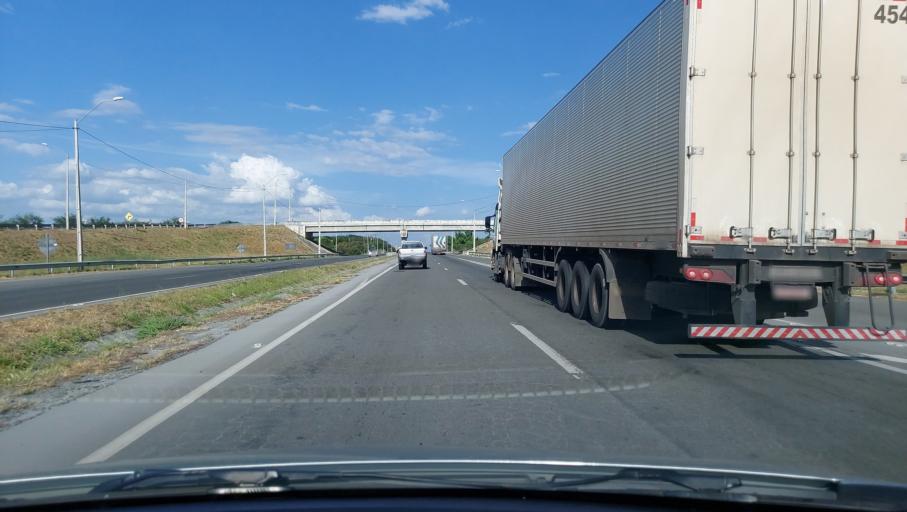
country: BR
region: Bahia
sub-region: Santo Estevao
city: Santo Estevao
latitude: -12.5029
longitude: -39.3561
